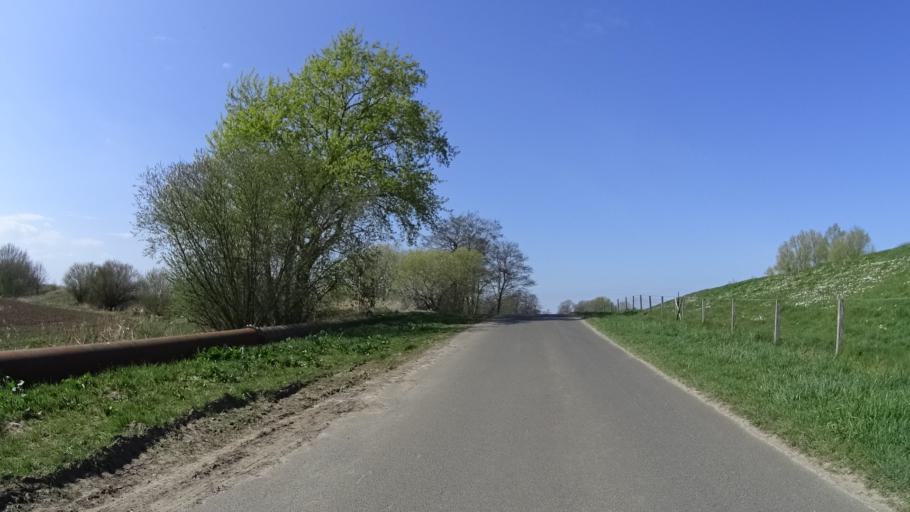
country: DE
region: Lower Saxony
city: Weener
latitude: 53.1009
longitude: 7.3314
